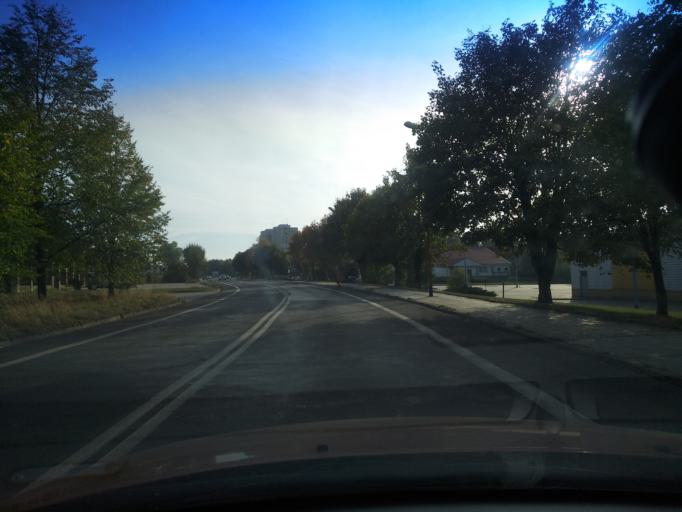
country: PL
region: Lower Silesian Voivodeship
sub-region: Powiat zgorzelecki
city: Zgorzelec
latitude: 51.1615
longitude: 15.0087
